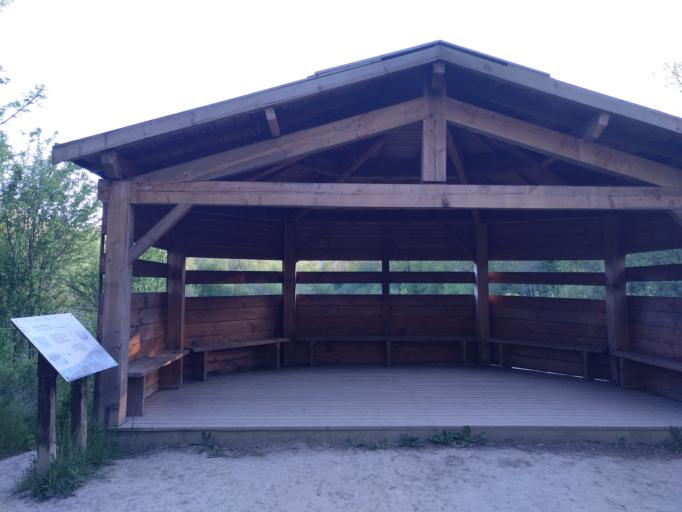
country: FR
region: Rhone-Alpes
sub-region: Departement du Rhone
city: Vernaison
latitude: 45.6381
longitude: 4.8119
